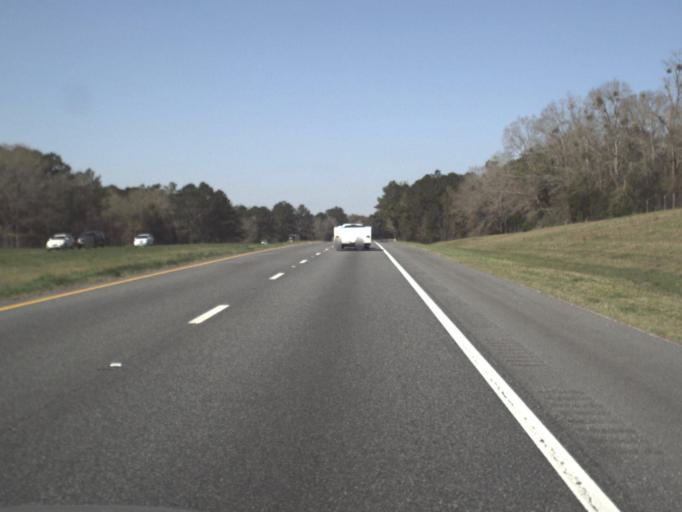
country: US
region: Florida
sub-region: Jackson County
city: Marianna
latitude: 30.7279
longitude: -85.2152
